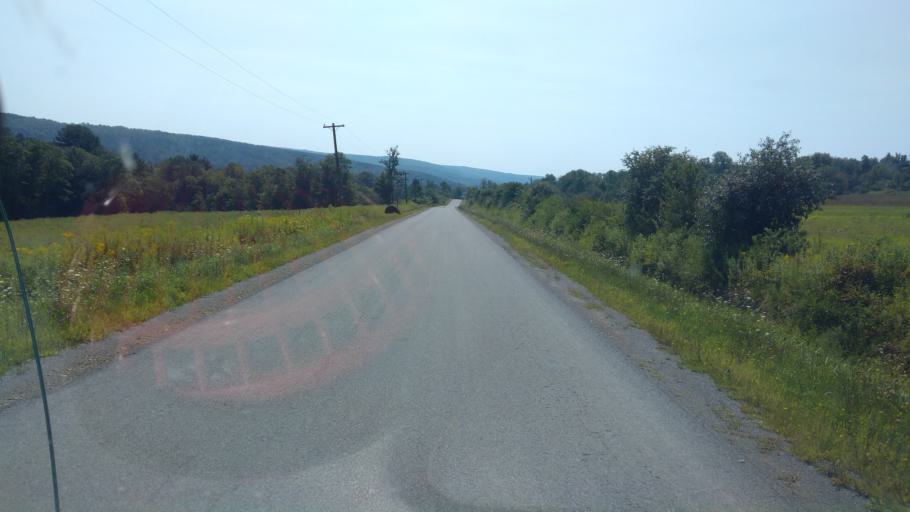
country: US
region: New York
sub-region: Allegany County
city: Belmont
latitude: 42.3381
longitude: -78.0404
